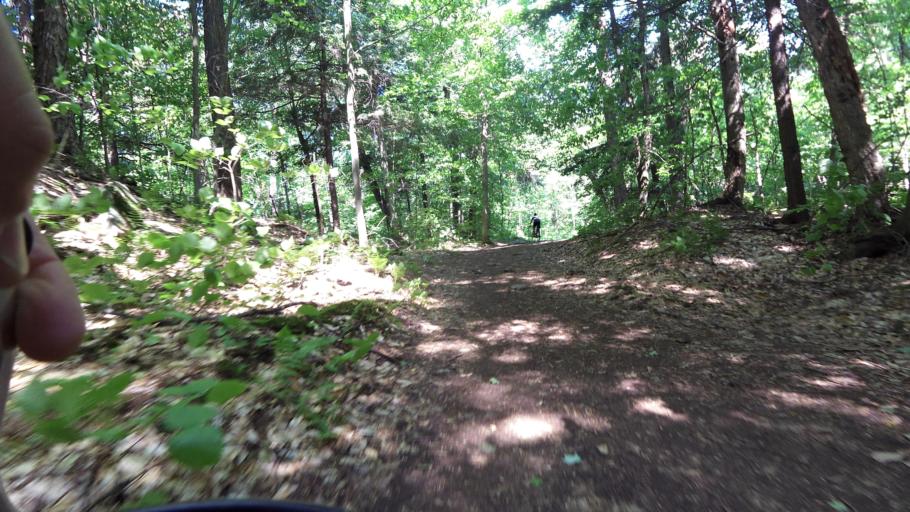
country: CA
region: Quebec
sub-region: Outaouais
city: Wakefield
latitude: 45.5380
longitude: -75.8739
